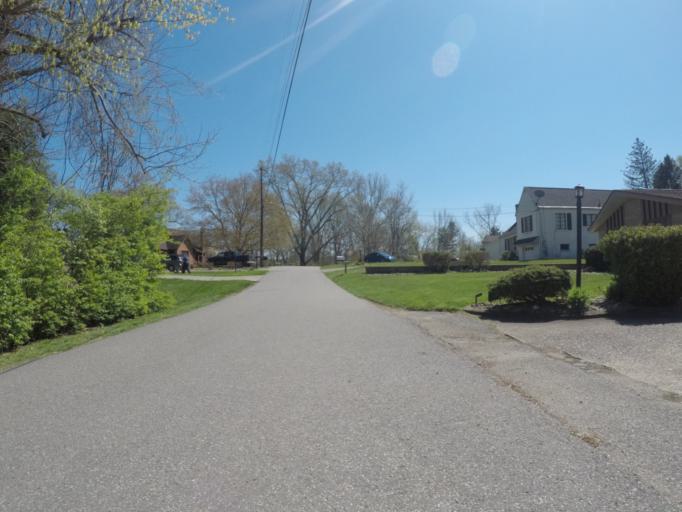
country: US
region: West Virginia
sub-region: Cabell County
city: Pea Ridge
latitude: 38.4183
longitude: -82.3160
